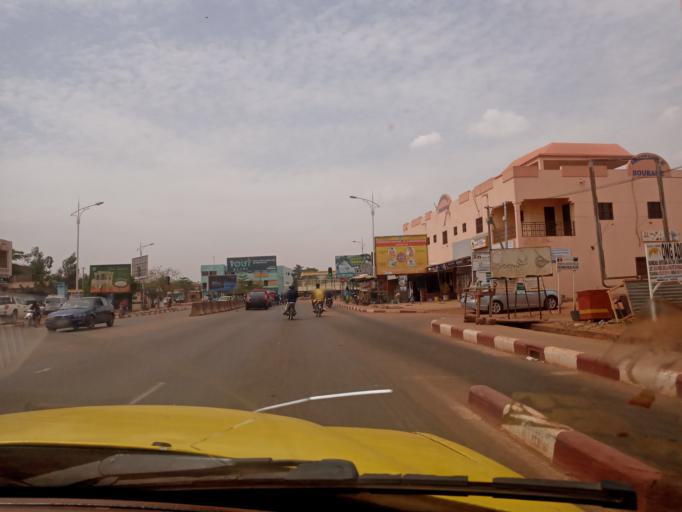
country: ML
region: Bamako
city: Bamako
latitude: 12.6653
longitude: -7.9318
